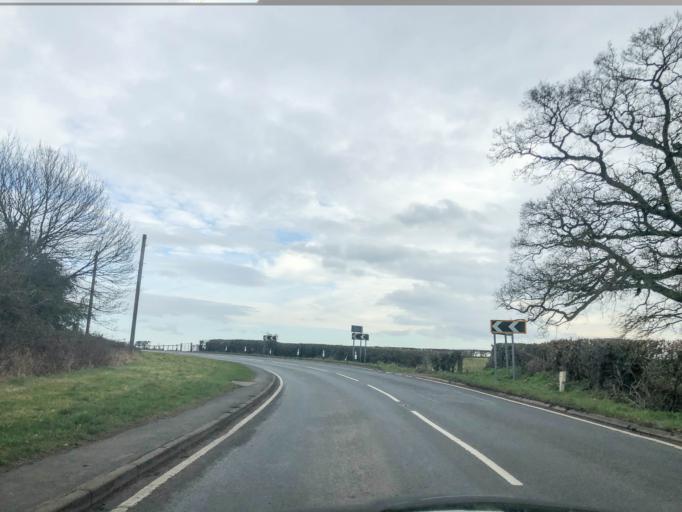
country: GB
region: England
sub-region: Warwickshire
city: Wroxall
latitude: 52.3029
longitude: -1.6780
